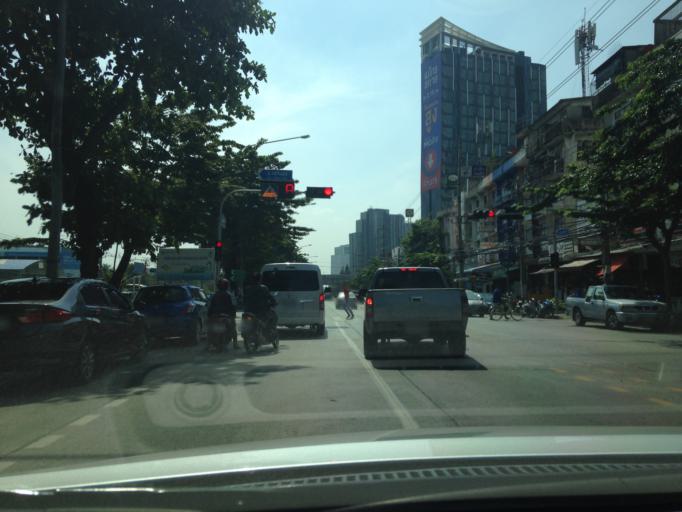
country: TH
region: Bangkok
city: Bang Sue
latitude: 13.8245
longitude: 100.5377
